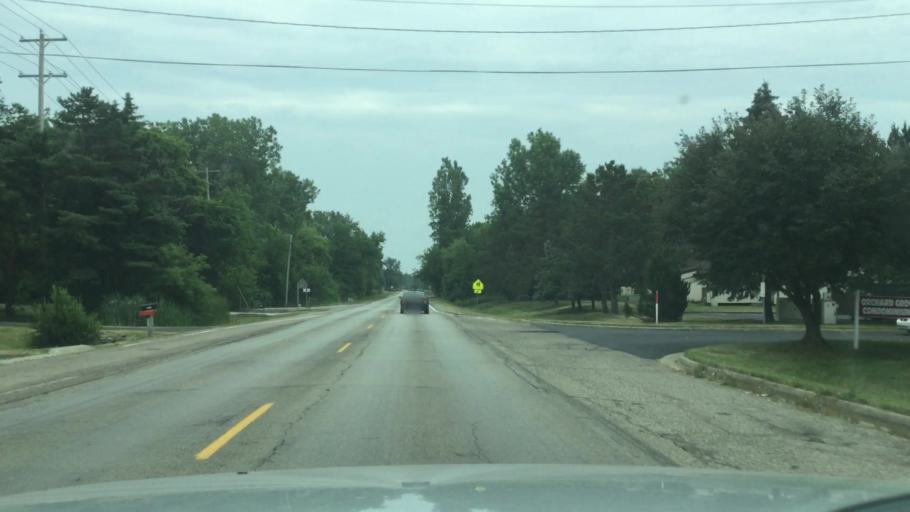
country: US
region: Michigan
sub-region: Genesee County
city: Flint
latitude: 42.9546
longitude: -83.7125
